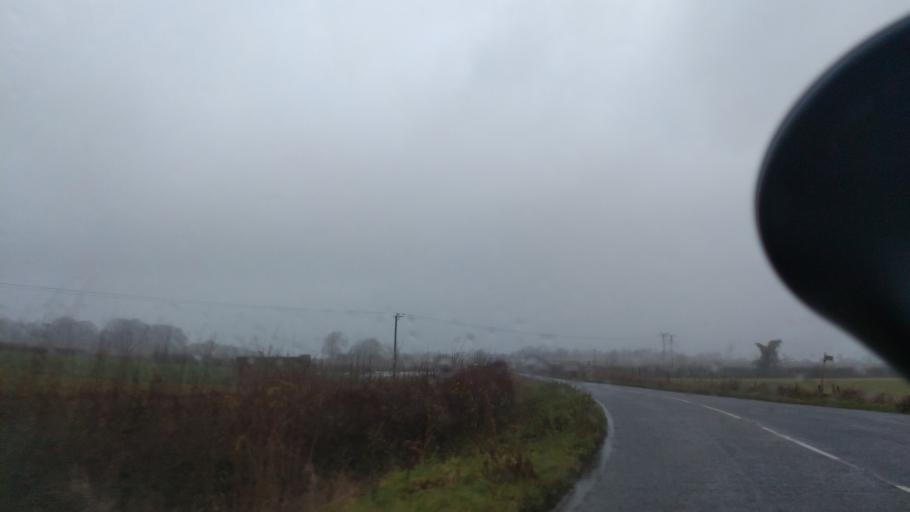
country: GB
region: England
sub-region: Wiltshire
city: Box
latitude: 51.3991
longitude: -2.2305
